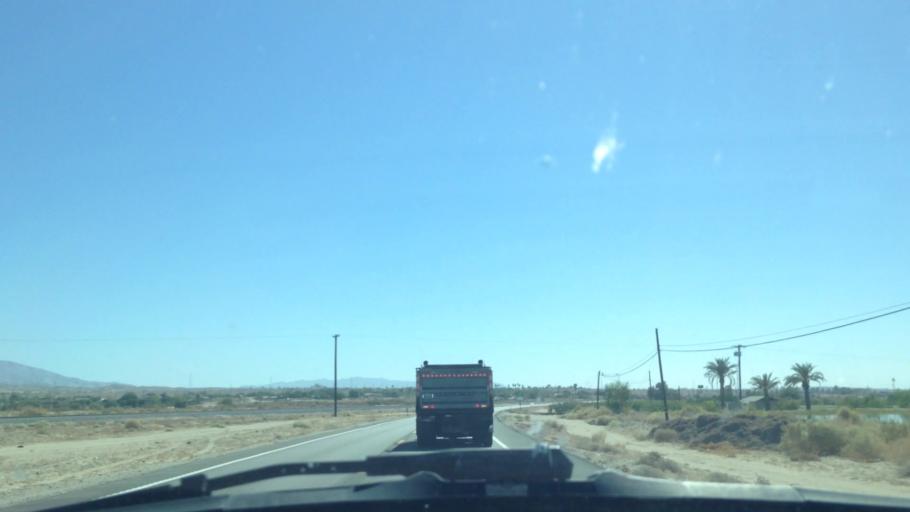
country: US
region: California
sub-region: Riverside County
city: Mecca
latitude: 33.5316
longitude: -115.9501
